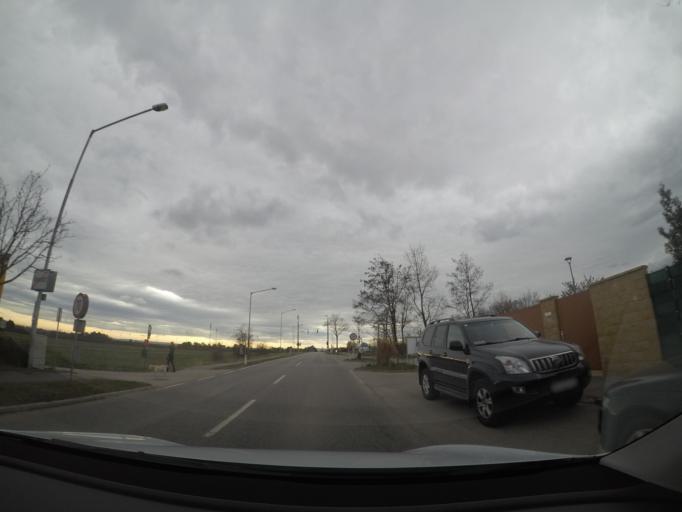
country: AT
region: Lower Austria
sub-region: Politischer Bezirk Modling
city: Vosendorf
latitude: 48.1194
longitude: 16.3316
